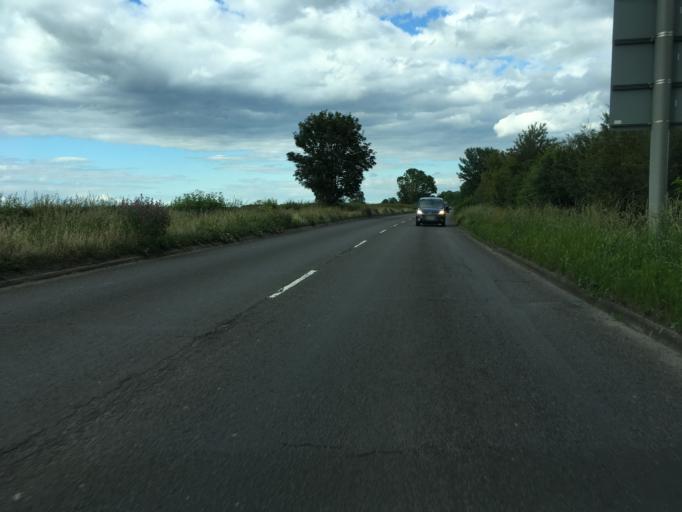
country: GB
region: England
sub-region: Buckinghamshire
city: Haddenham
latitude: 51.7778
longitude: -0.9451
